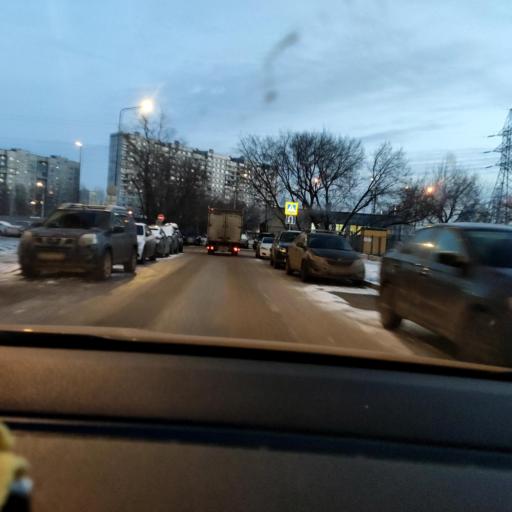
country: RU
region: Moskovskaya
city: Kur'yanovo
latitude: 55.6451
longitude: 37.7062
